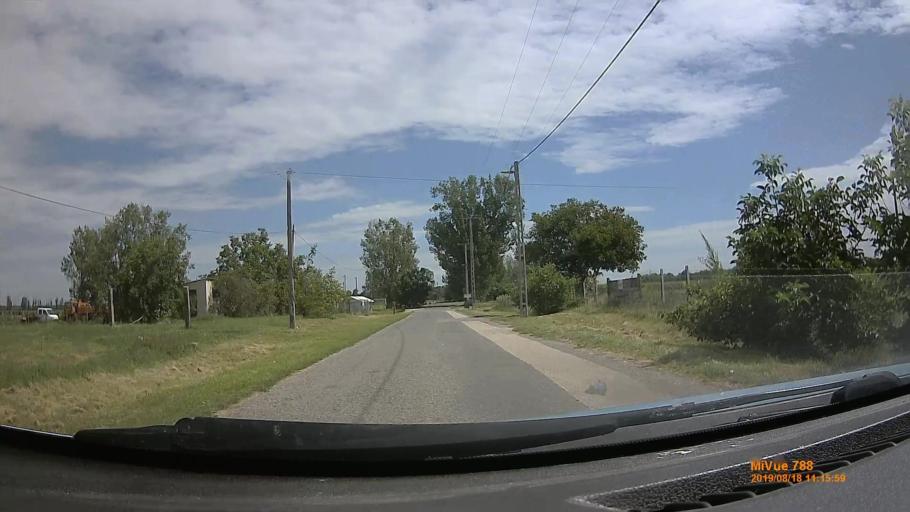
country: HU
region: Fejer
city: Szabadbattyan
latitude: 47.0848
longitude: 18.4081
